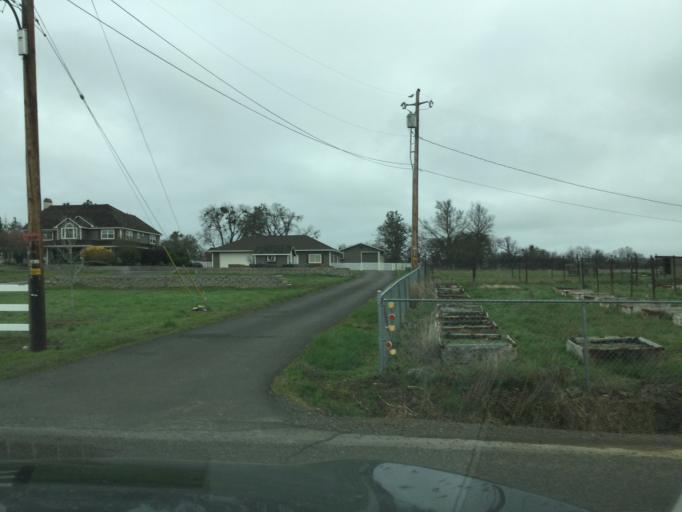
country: US
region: Oregon
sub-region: Jackson County
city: Central Point
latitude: 42.4077
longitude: -122.9089
